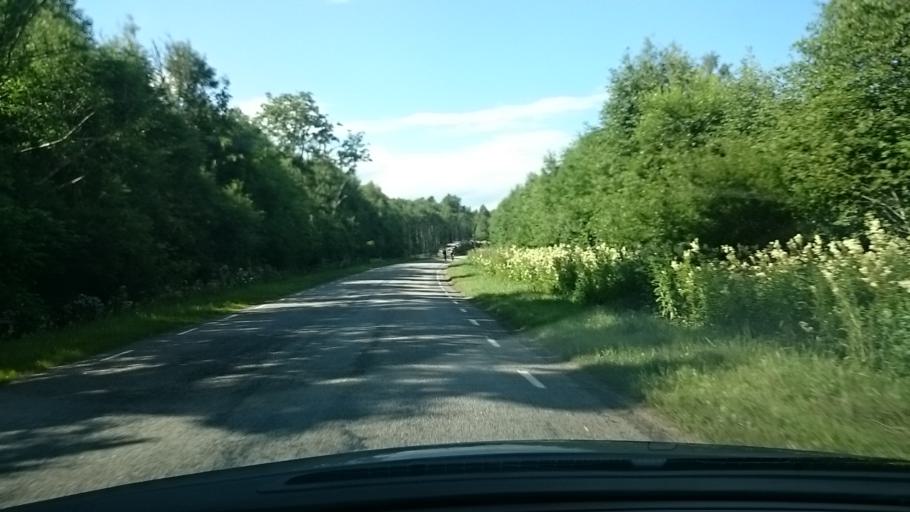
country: EE
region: Laeaene
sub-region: Haapsalu linn
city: Haapsalu
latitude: 59.0739
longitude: 23.5684
